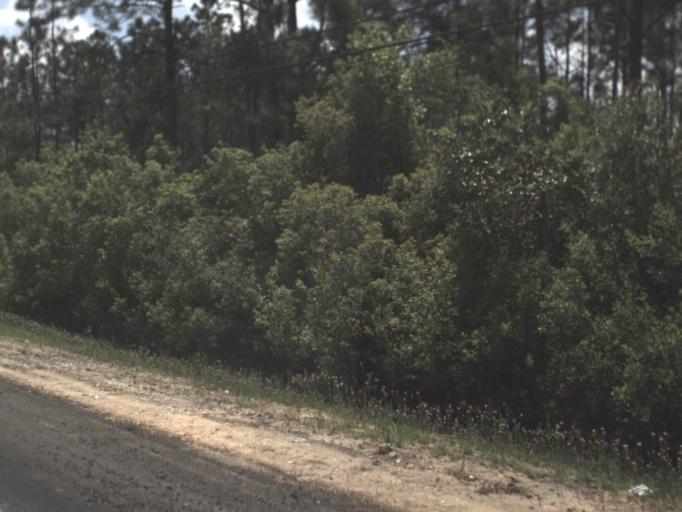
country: US
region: Florida
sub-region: Escambia County
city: Myrtle Grove
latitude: 30.3948
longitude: -87.3144
